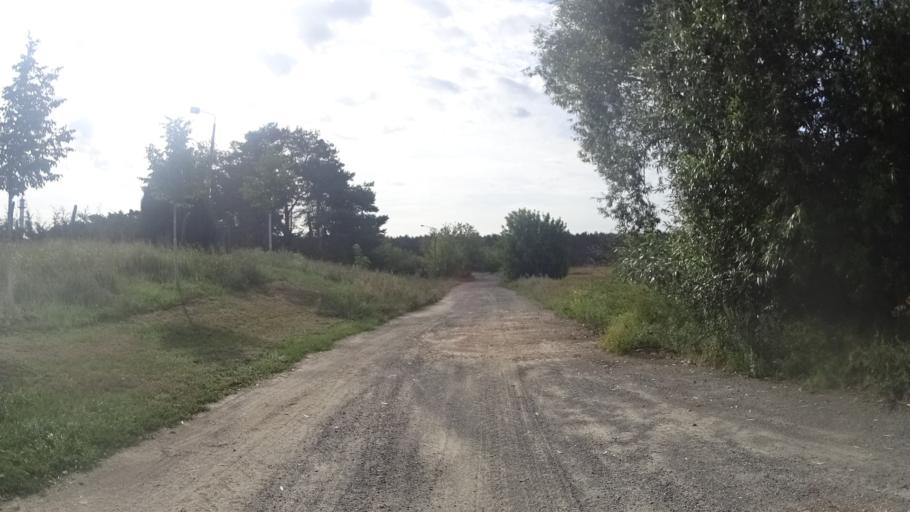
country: DE
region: Brandenburg
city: Brandenburg an der Havel
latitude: 52.3783
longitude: 12.6207
